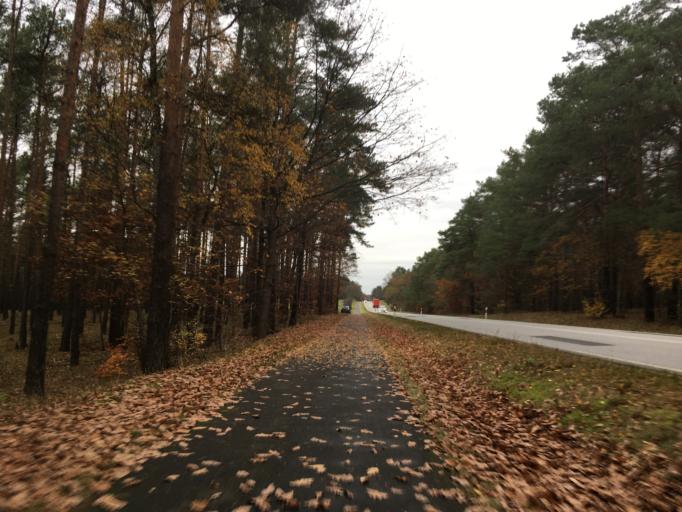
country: DE
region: Brandenburg
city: Mixdorf
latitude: 52.1979
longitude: 14.4597
